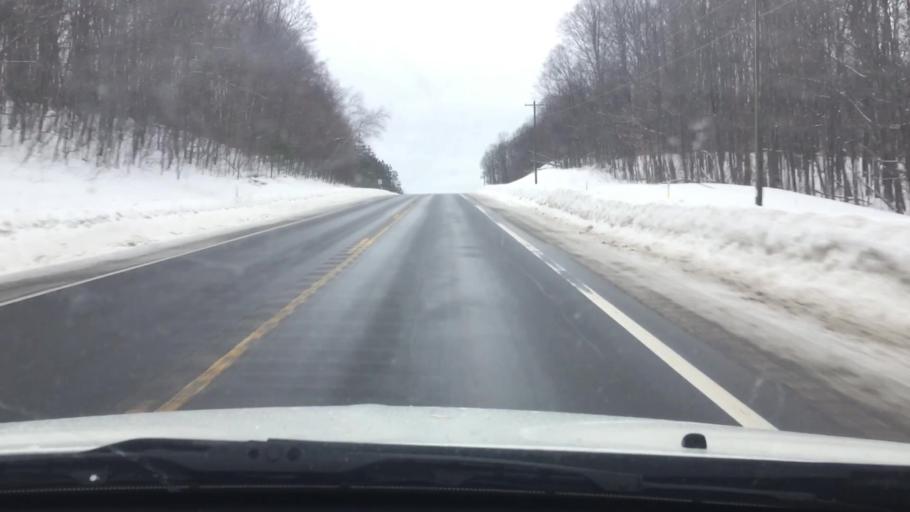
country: US
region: Michigan
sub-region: Charlevoix County
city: Boyne City
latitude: 45.0964
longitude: -85.0086
